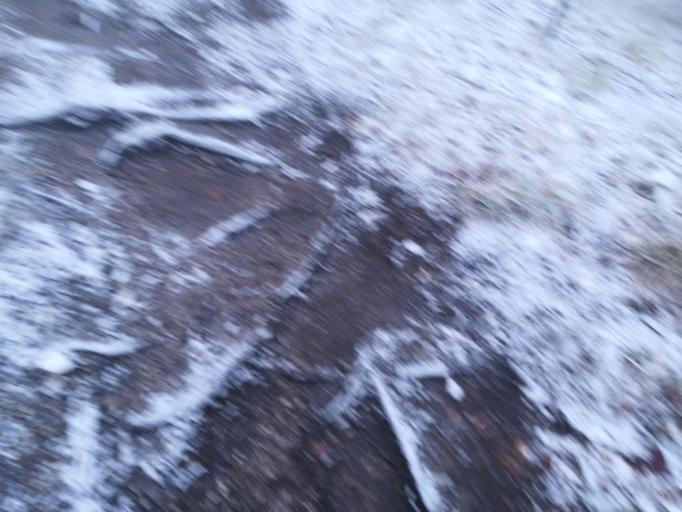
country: HR
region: Varazdinska
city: Ivanec
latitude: 46.1850
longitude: 16.1407
